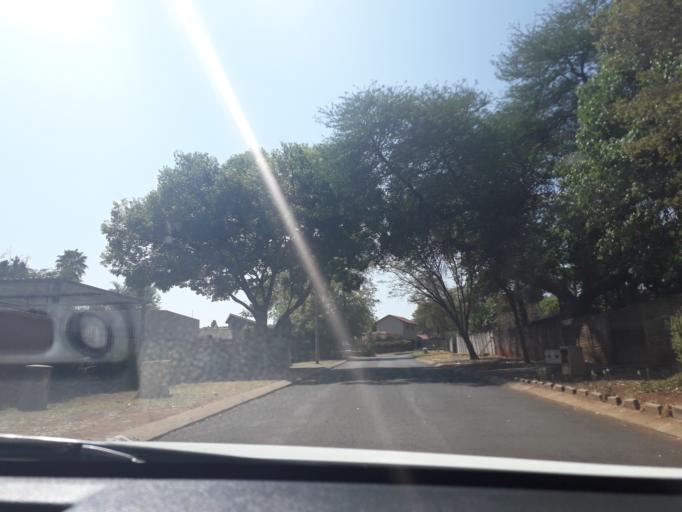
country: ZA
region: Gauteng
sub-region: City of Johannesburg Metropolitan Municipality
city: Roodepoort
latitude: -26.1305
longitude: 27.9349
